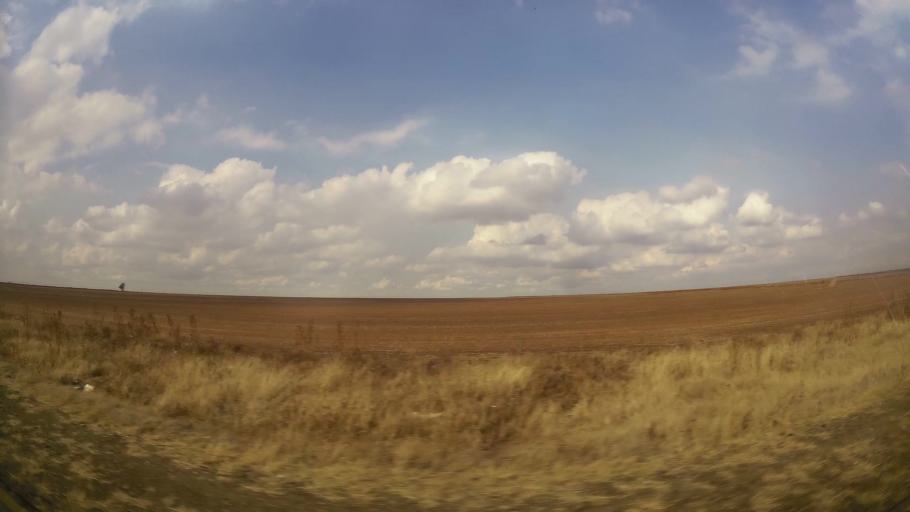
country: ZA
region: Orange Free State
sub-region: Fezile Dabi District Municipality
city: Sasolburg
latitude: -26.8373
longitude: 27.8951
